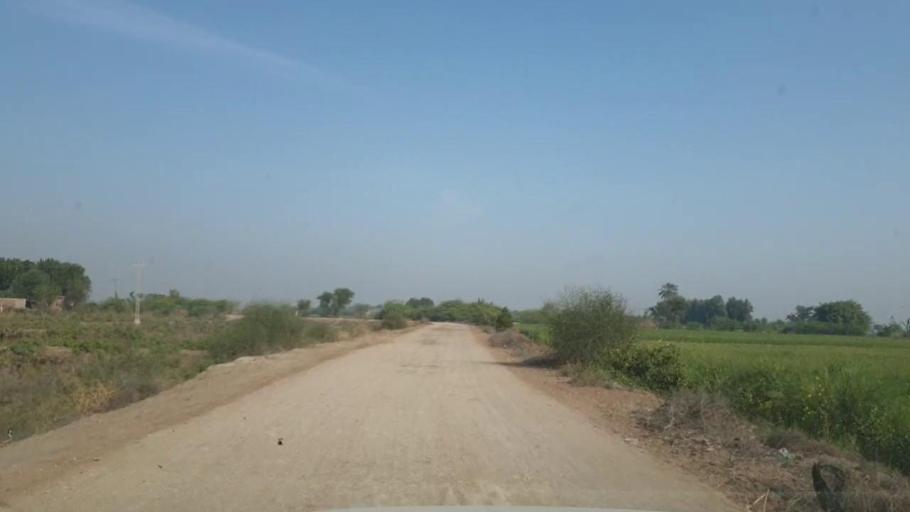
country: PK
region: Sindh
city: Mirpur Khas
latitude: 25.5096
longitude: 69.0391
